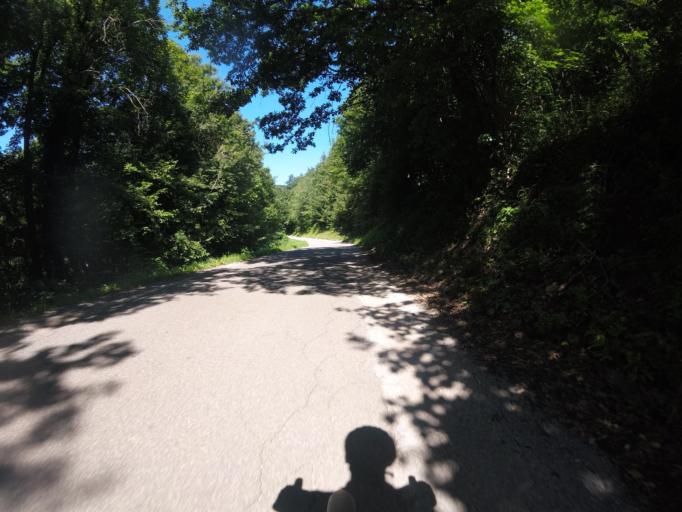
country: SI
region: Kostanjevica na Krki
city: Kostanjevica na Krki
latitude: 45.8196
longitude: 15.5239
